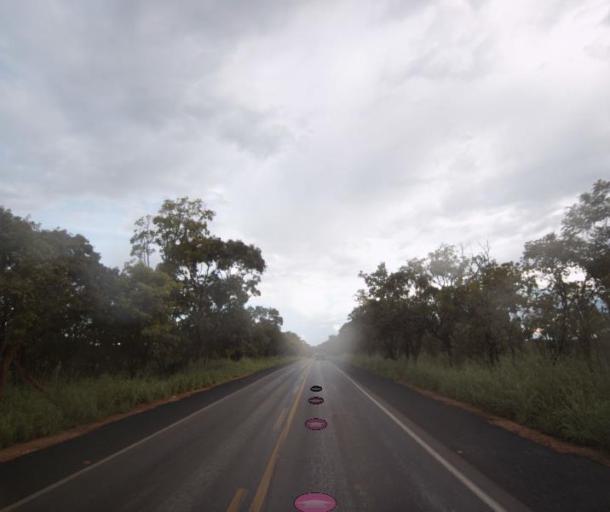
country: BR
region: Goias
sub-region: Porangatu
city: Porangatu
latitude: -13.9026
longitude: -49.0615
